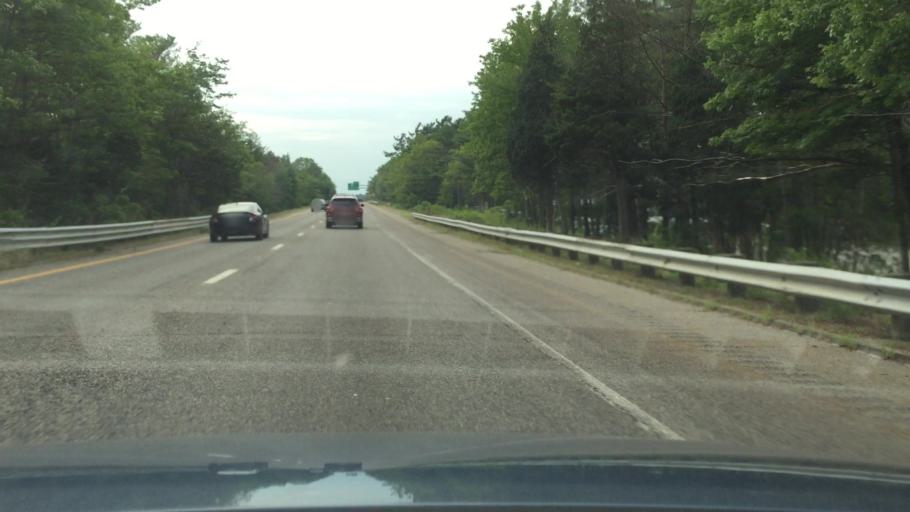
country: US
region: Massachusetts
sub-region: Plymouth County
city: North Pembroke
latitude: 42.1060
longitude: -70.7633
